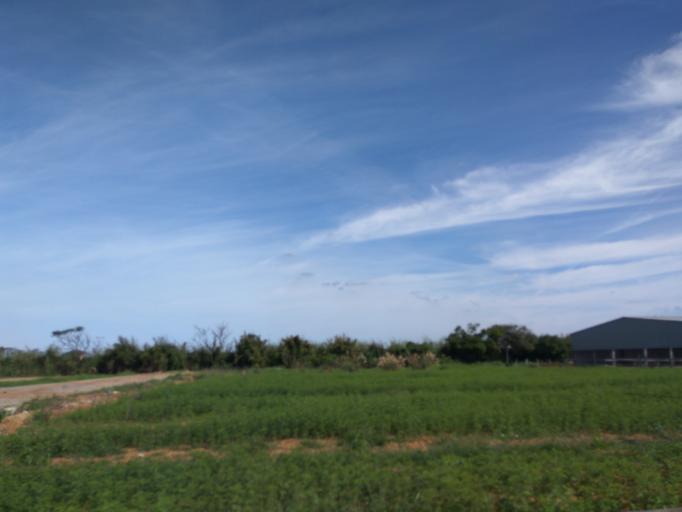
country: TW
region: Taiwan
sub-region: Hsinchu
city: Zhubei
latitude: 25.0158
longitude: 121.0876
